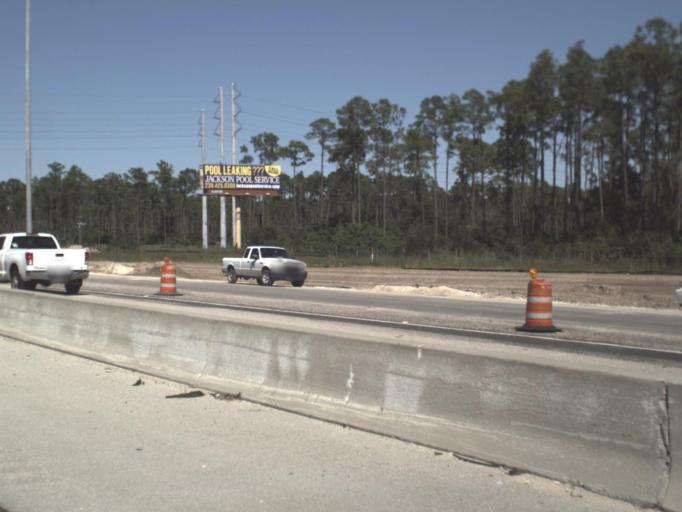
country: US
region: Florida
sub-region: Lee County
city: Three Oaks
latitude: 26.4984
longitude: -81.7943
